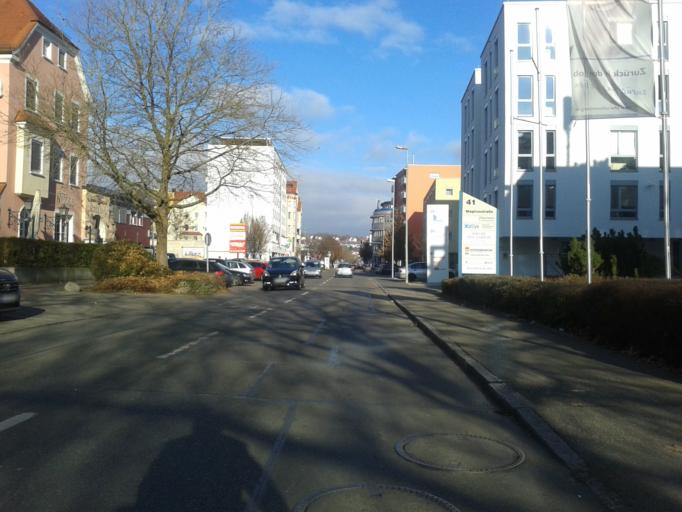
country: DE
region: Baden-Wuerttemberg
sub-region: Tuebingen Region
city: Ulm
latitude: 48.3931
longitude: 9.9641
